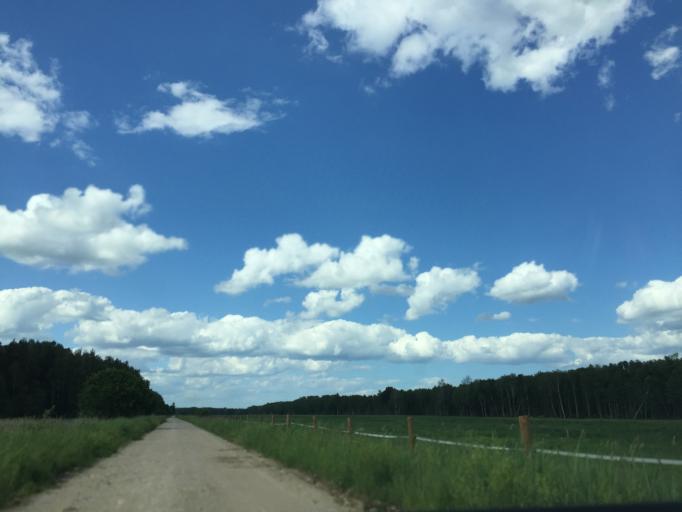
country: LV
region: Engure
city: Smarde
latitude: 56.8447
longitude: 23.3987
